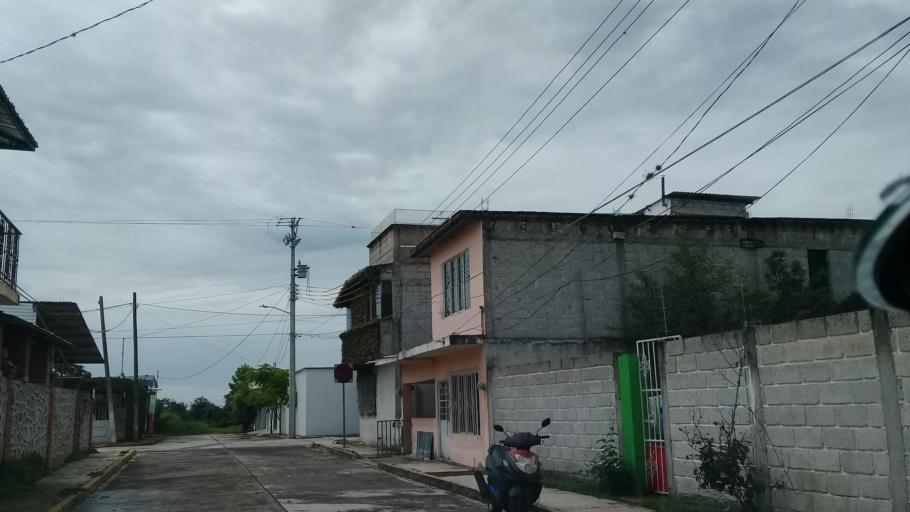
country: MX
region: Veracruz
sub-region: Emiliano Zapata
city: Dos Rios
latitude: 19.4800
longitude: -96.7979
